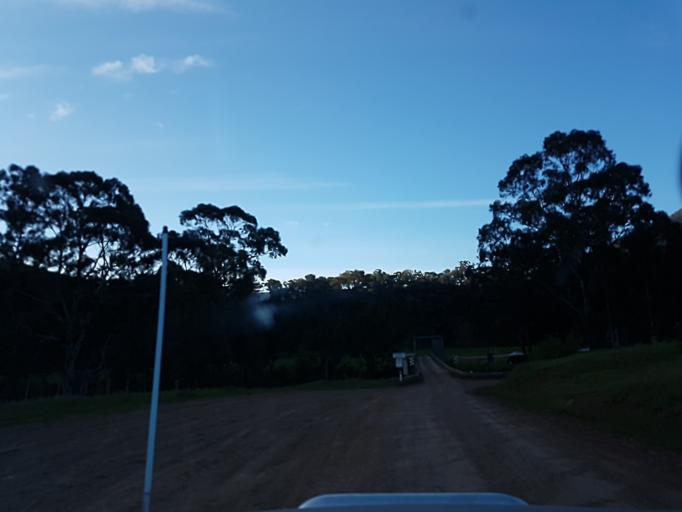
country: AU
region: Victoria
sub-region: East Gippsland
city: Bairnsdale
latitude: -37.4110
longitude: 147.1156
